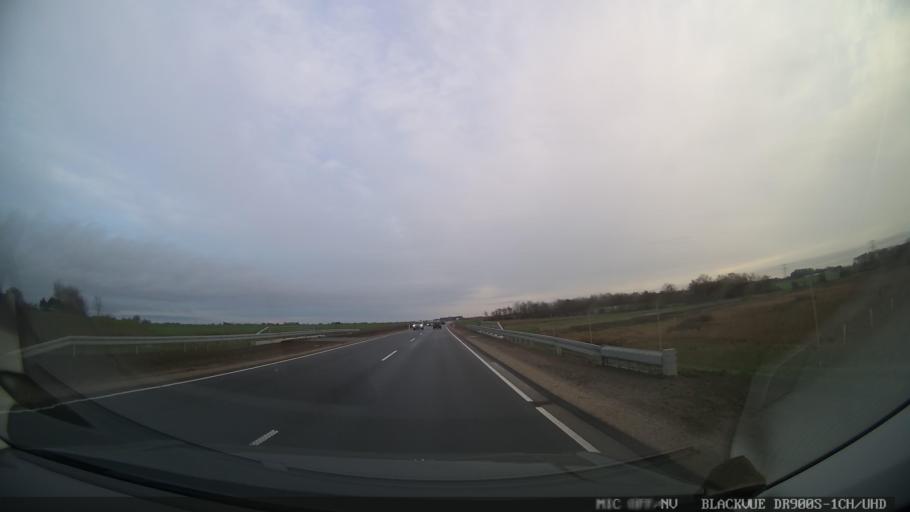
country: DK
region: Central Jutland
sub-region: Arhus Kommune
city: Tranbjerg
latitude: 56.0763
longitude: 10.1283
